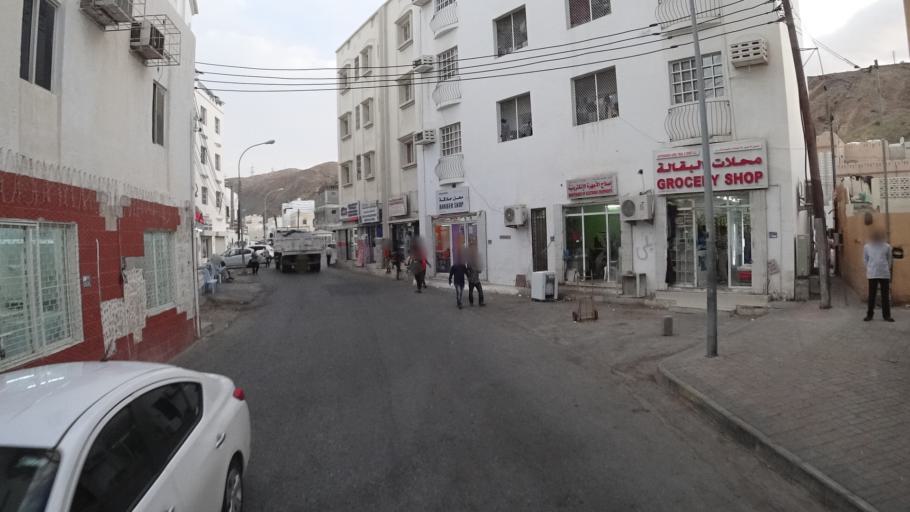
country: OM
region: Muhafazat Masqat
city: Muscat
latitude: 23.5805
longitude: 58.5455
